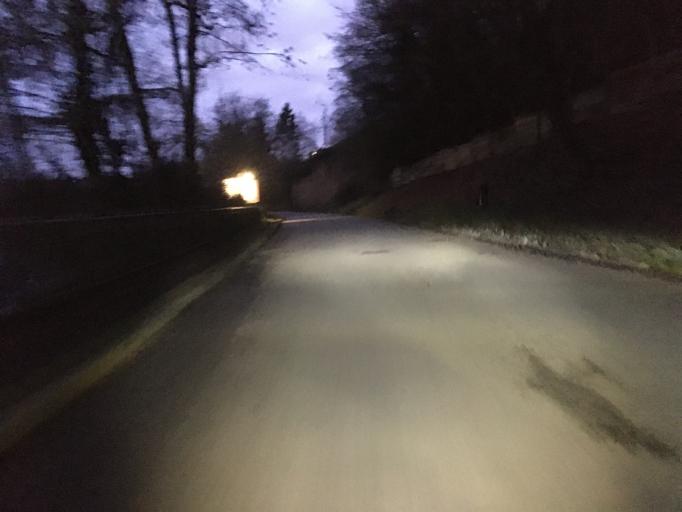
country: DE
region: Baden-Wuerttemberg
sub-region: Regierungsbezirk Stuttgart
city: Stuttgart Muehlhausen
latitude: 48.8283
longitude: 9.2075
